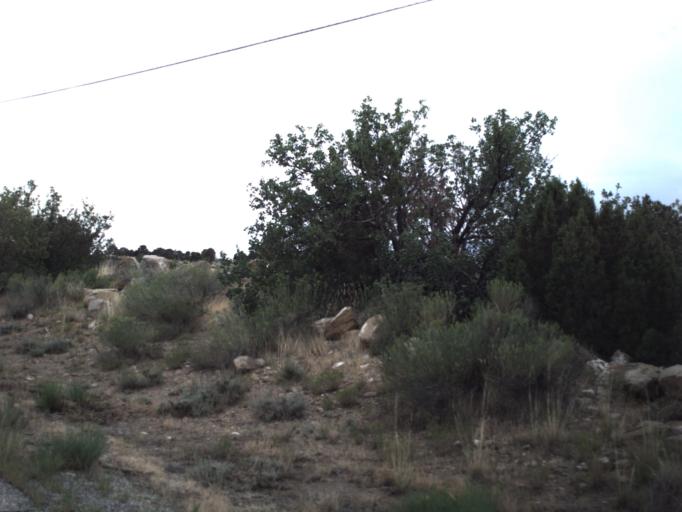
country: US
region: Utah
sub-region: Carbon County
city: East Carbon City
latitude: 39.5351
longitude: -110.4040
